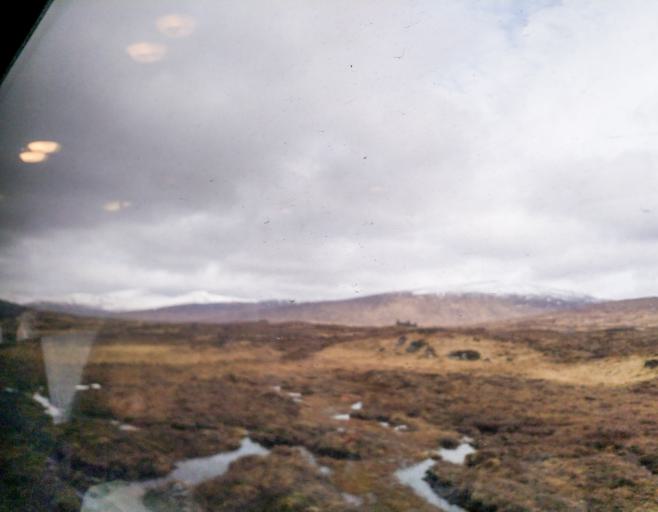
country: GB
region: Scotland
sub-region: Highland
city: Spean Bridge
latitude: 56.7382
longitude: -4.6598
